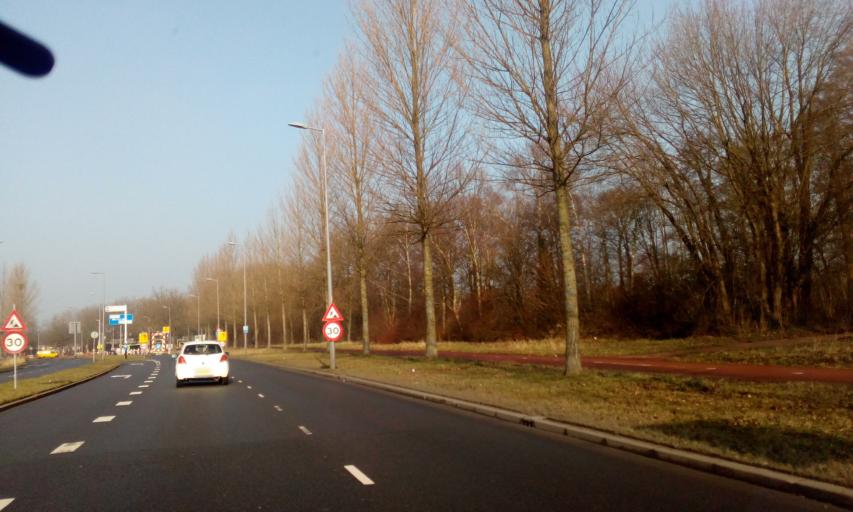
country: NL
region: South Holland
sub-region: Gemeente Barendrecht
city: Barendrecht
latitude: 51.8801
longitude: 4.5384
